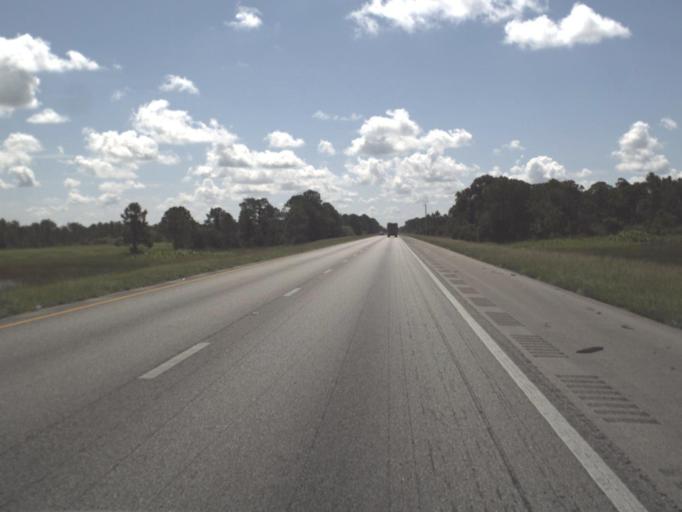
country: US
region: Florida
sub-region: Lee County
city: Burnt Store Marina
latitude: 26.8271
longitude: -81.9510
